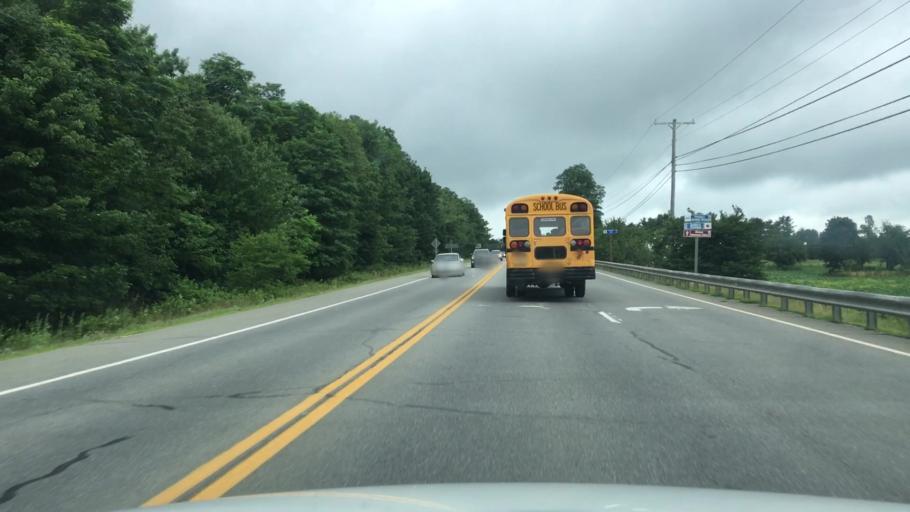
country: US
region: Maine
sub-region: Kennebec County
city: Windsor
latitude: 44.2774
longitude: -69.5952
